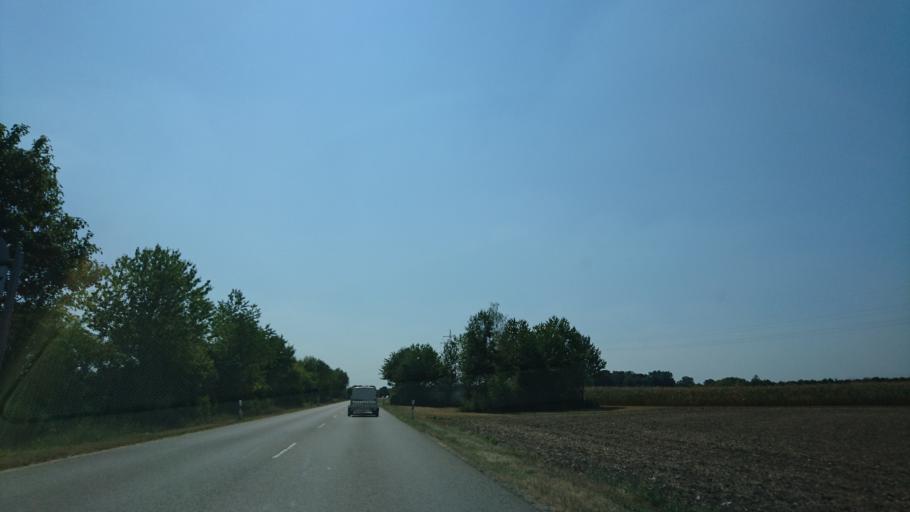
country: DE
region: Bavaria
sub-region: Swabia
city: Friedberg
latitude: 48.3434
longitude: 10.9625
